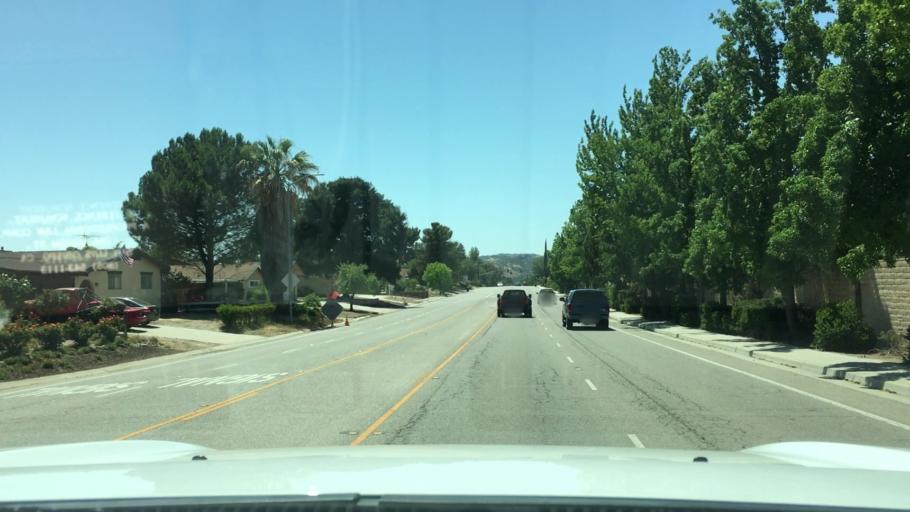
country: US
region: California
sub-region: San Luis Obispo County
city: Paso Robles
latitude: 35.6158
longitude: -120.6602
